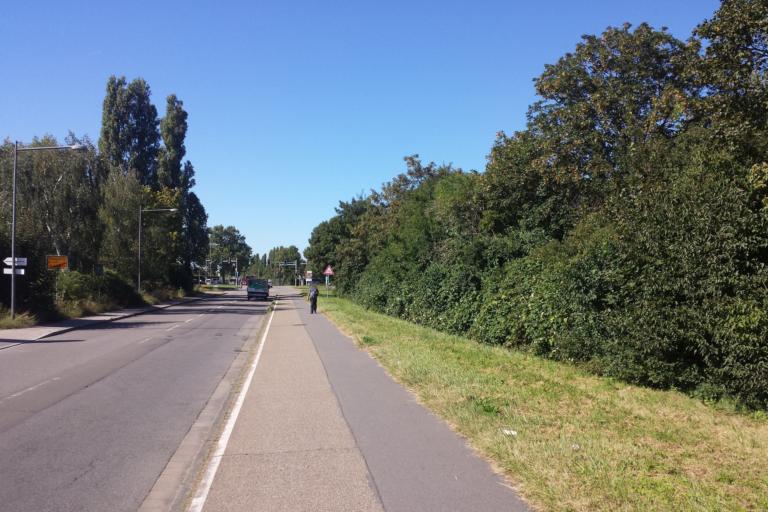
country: DE
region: Baden-Wuerttemberg
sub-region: Karlsruhe Region
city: Eppelheim
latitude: 49.3872
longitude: 8.6624
